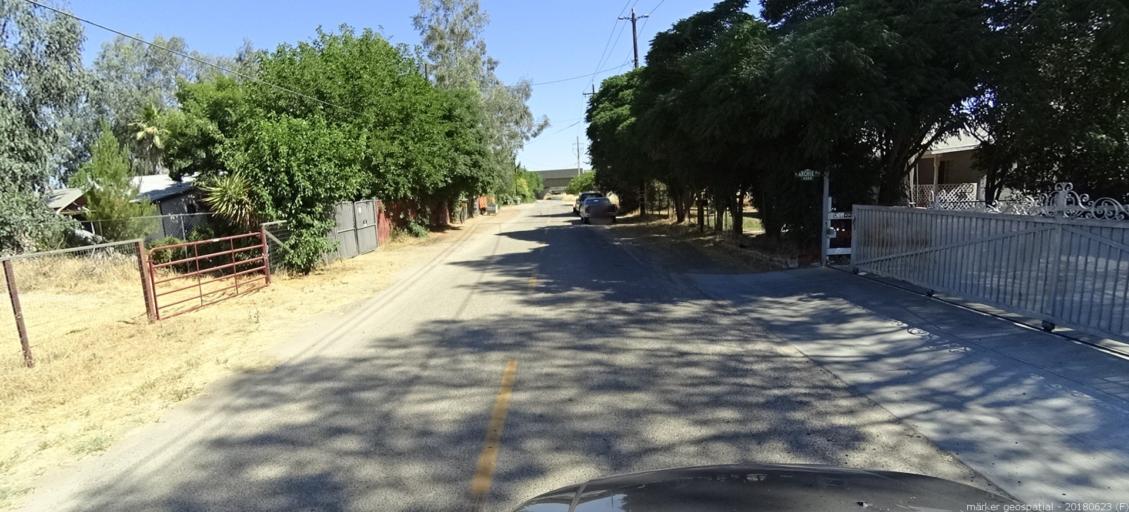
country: US
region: California
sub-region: Madera County
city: Parksdale
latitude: 36.9802
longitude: -120.0264
